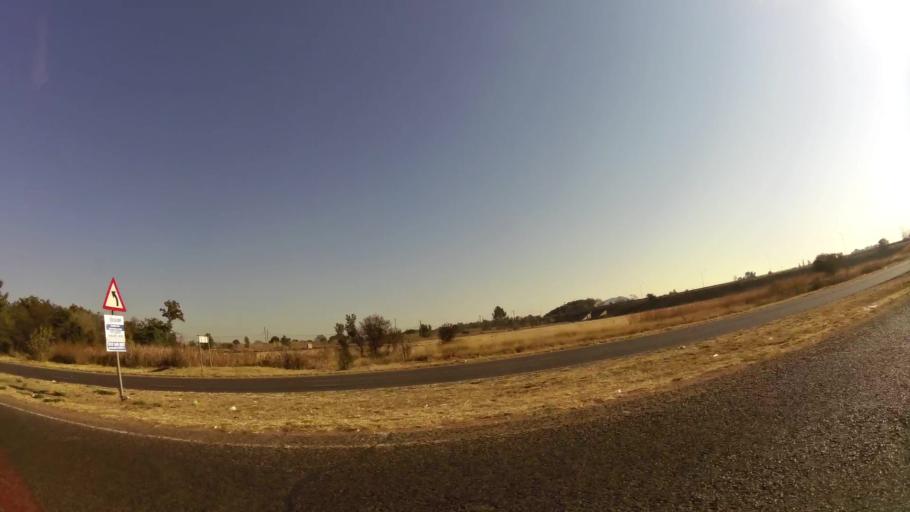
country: ZA
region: Gauteng
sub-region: City of Tshwane Metropolitan Municipality
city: Pretoria
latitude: -25.6603
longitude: 28.1851
